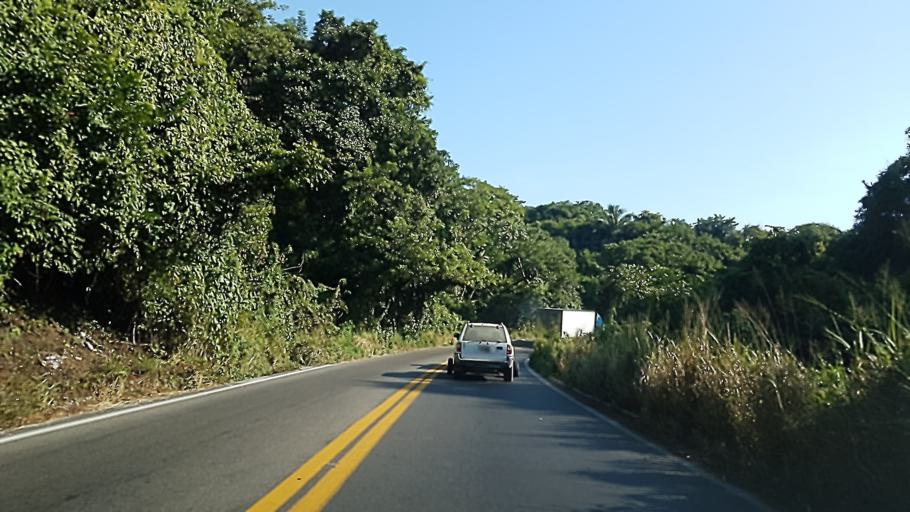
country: MX
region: Nayarit
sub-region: Bahia de Banderas
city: Lo de Marcos
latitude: 20.9252
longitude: -105.3635
